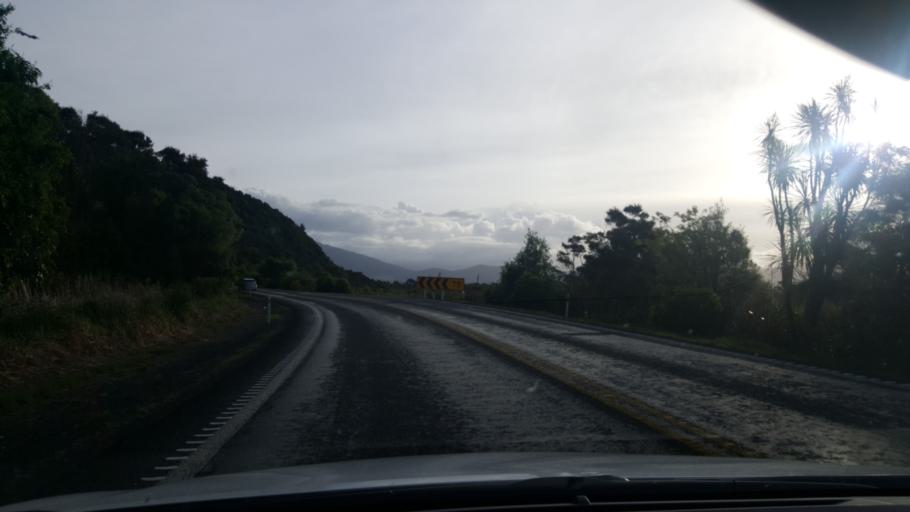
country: NZ
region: Waikato
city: Turangi
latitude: -38.9394
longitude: 175.8590
